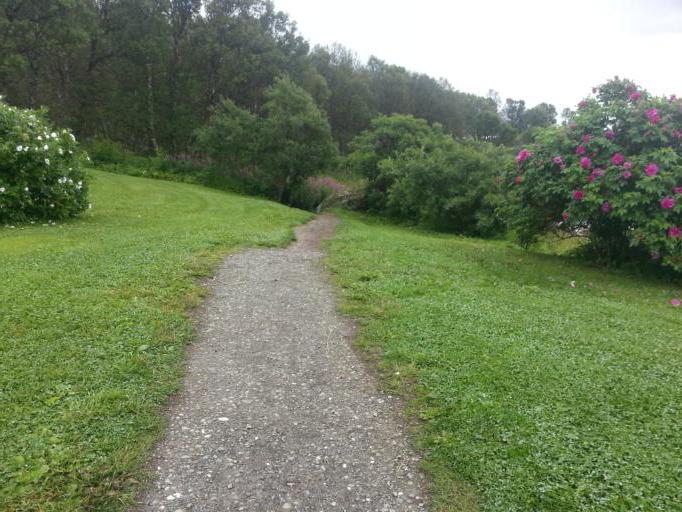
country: NO
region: Troms
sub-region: Tromso
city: Tromso
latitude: 69.6340
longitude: 18.9046
